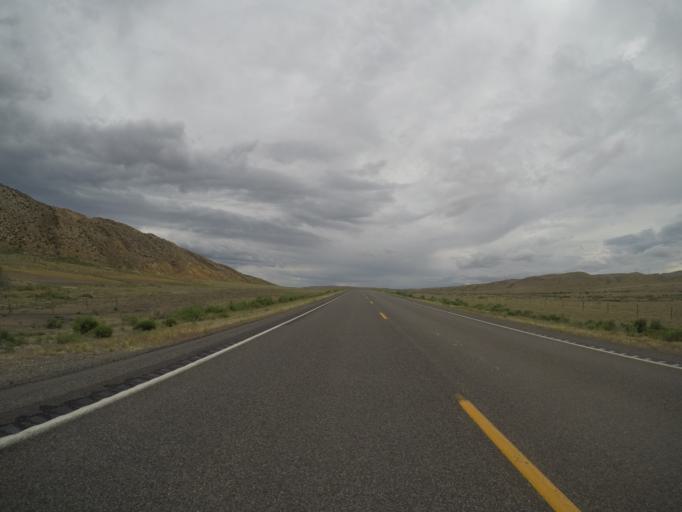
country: US
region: Wyoming
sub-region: Big Horn County
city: Lovell
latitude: 44.9448
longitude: -108.2968
